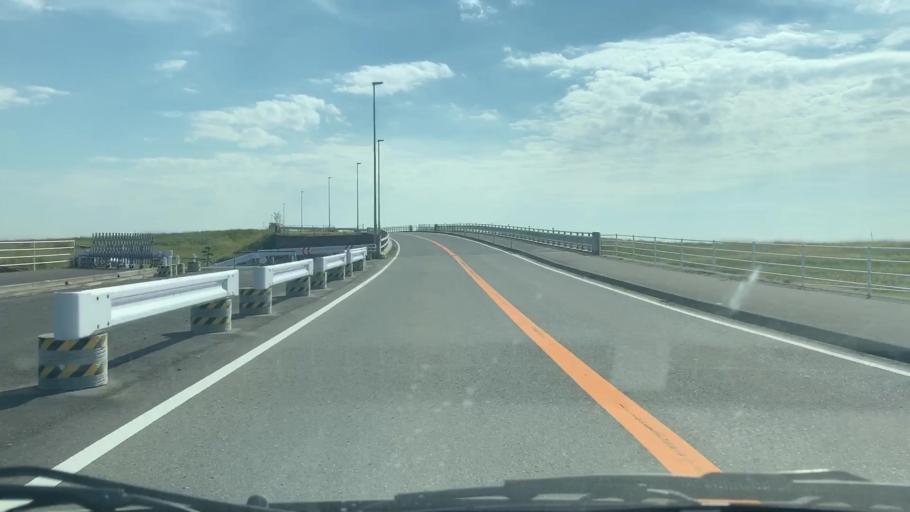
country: JP
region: Saga Prefecture
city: Saga-shi
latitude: 33.2232
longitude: 130.1917
